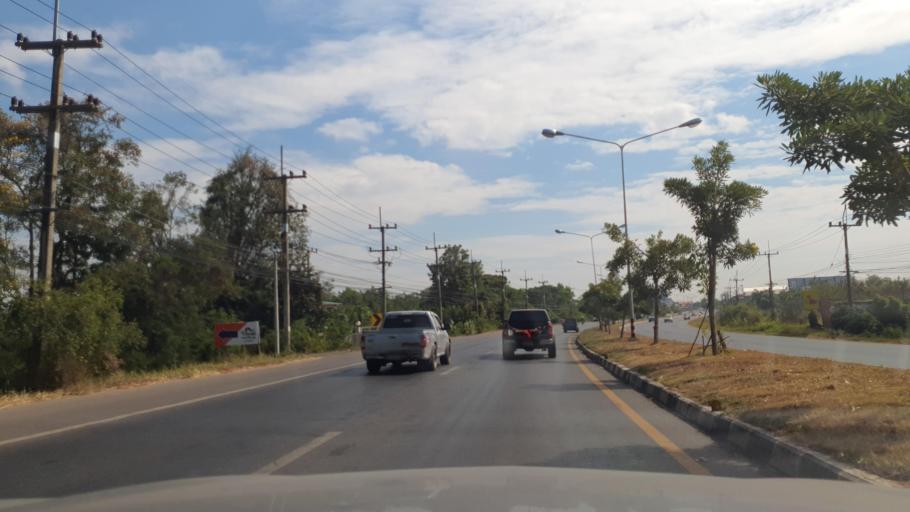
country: TH
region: Kalasin
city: Yang Talat
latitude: 16.4056
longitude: 103.4257
